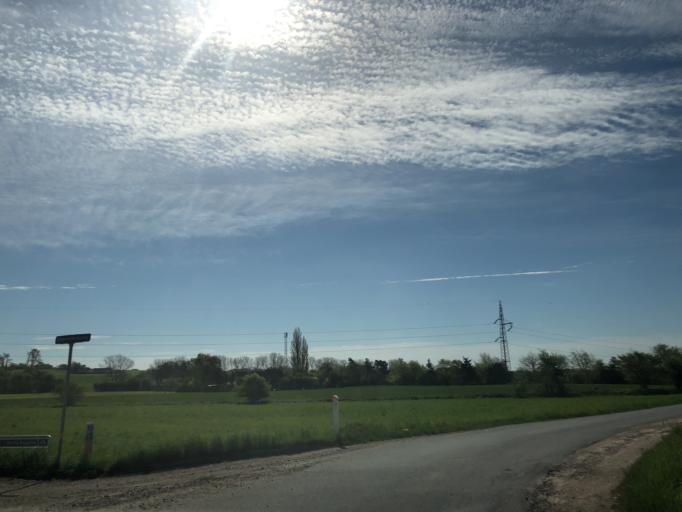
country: DK
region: Zealand
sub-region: Slagelse Kommune
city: Forlev
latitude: 55.3856
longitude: 11.2874
